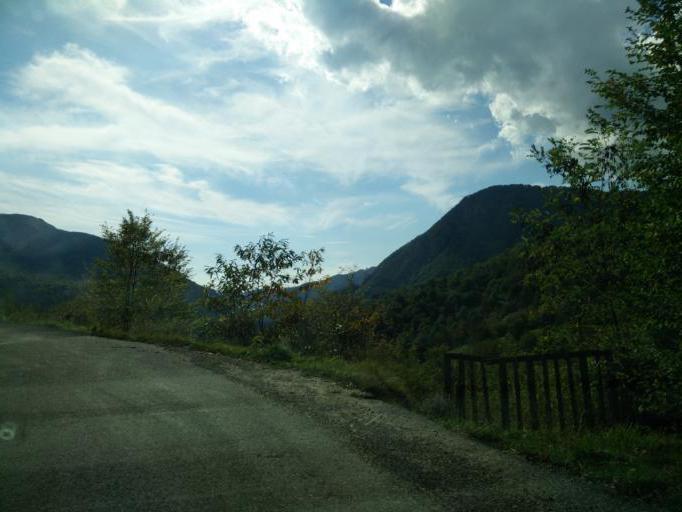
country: IT
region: Tuscany
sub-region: Provincia di Massa-Carrara
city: Patigno
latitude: 44.3576
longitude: 9.7282
